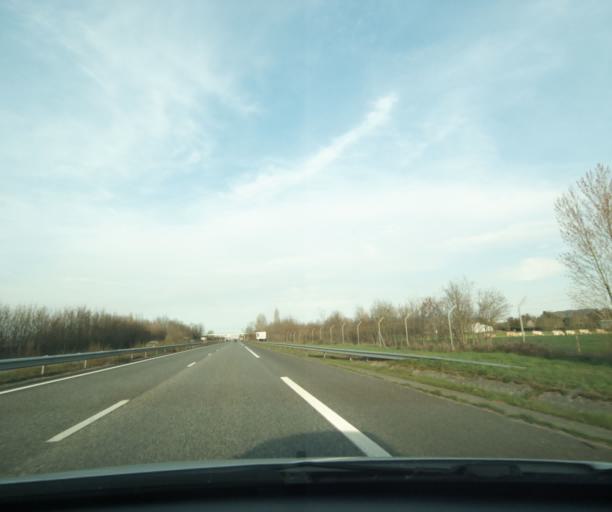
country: FR
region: Midi-Pyrenees
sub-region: Departement de la Haute-Garonne
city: Martres-Tolosane
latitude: 43.1985
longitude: 0.9998
